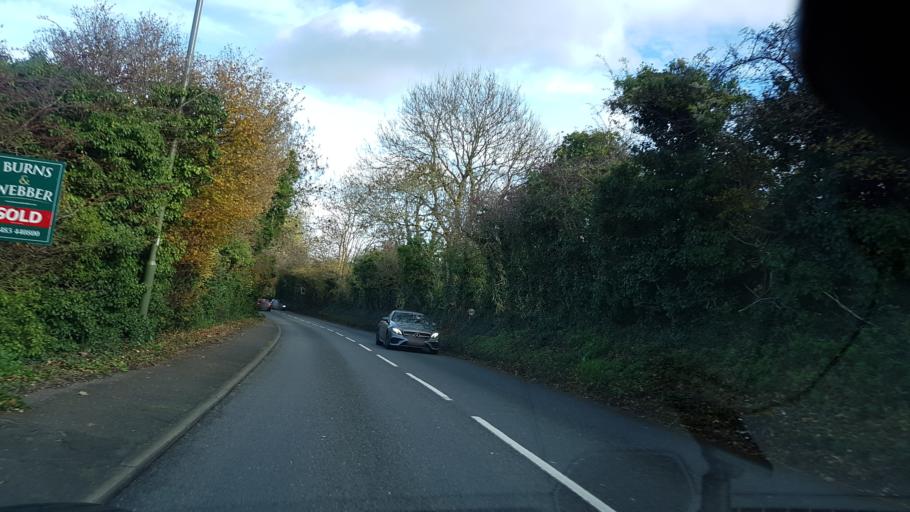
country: GB
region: England
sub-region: Surrey
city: Guildford
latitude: 51.2308
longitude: -0.6003
